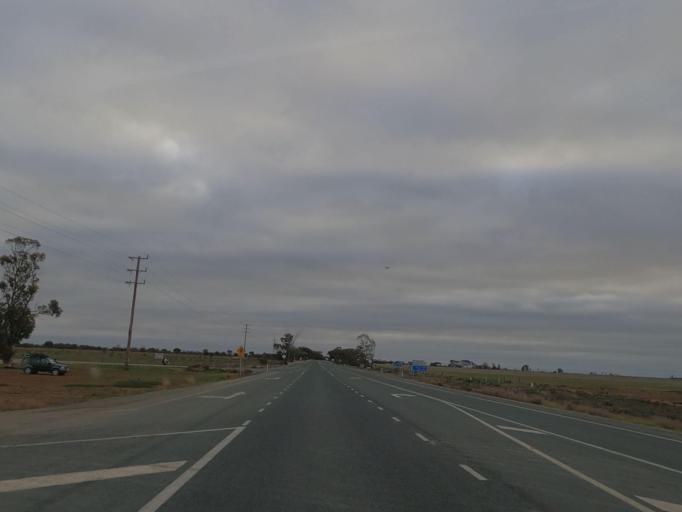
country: AU
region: Victoria
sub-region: Swan Hill
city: Swan Hill
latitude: -35.5518
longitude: 143.7707
